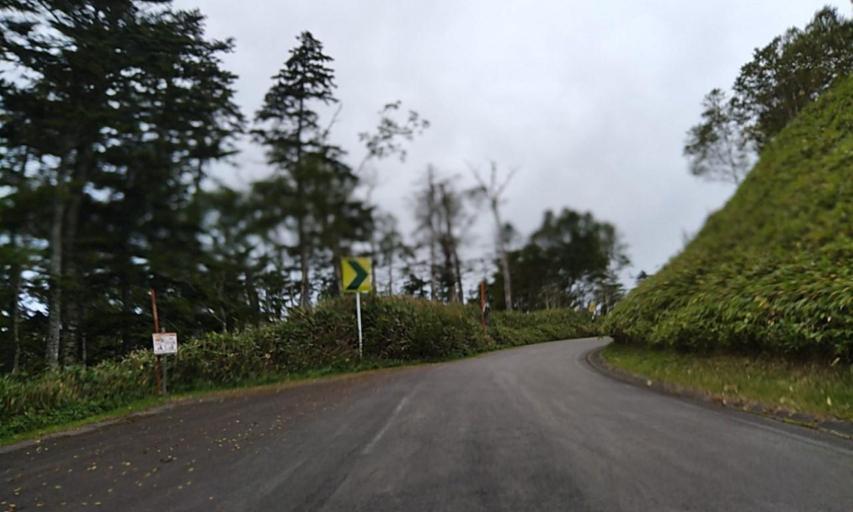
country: JP
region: Hokkaido
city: Bihoro
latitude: 43.5768
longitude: 144.2236
